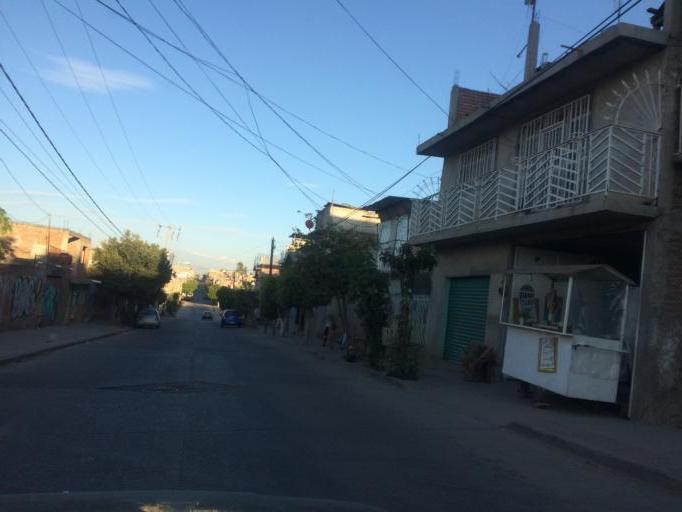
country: MX
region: Guanajuato
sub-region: Leon
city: La Ermita
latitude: 21.1382
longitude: -101.7164
